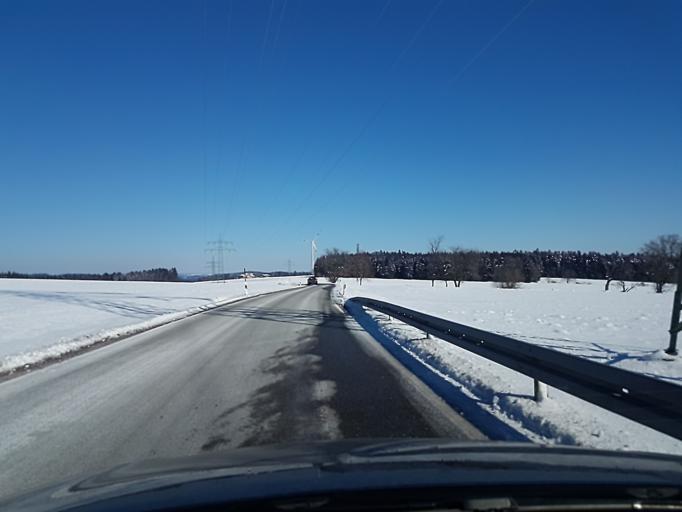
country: DE
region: Baden-Wuerttemberg
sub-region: Freiburg Region
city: Tennenbronn
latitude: 48.1624
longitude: 8.3528
